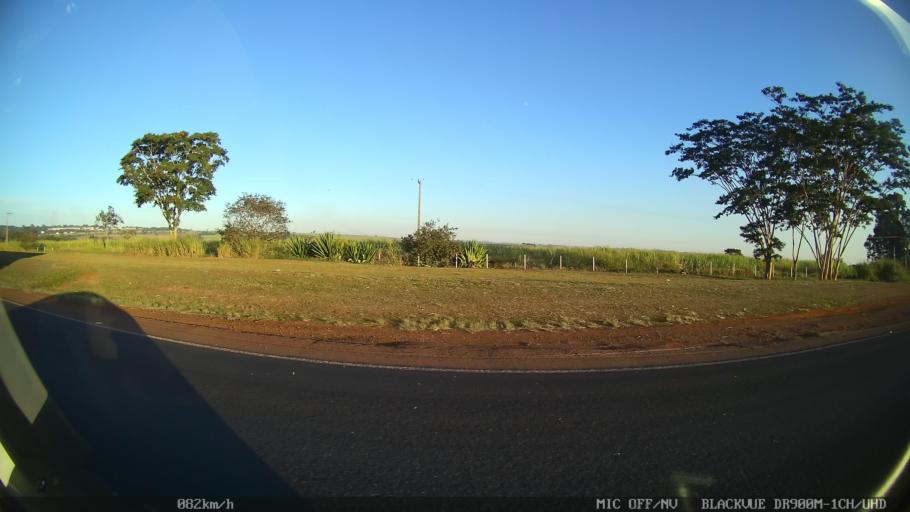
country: BR
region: Sao Paulo
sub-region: Araraquara
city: Araraquara
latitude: -21.8170
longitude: -48.2035
